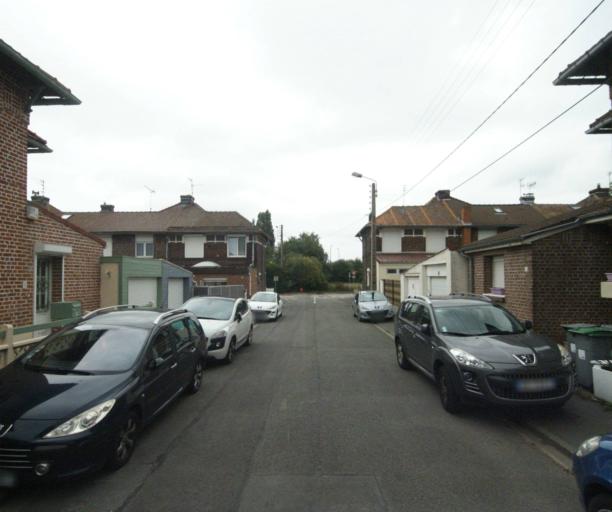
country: FR
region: Nord-Pas-de-Calais
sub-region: Departement du Nord
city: Wattrelos
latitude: 50.6847
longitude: 3.2242
